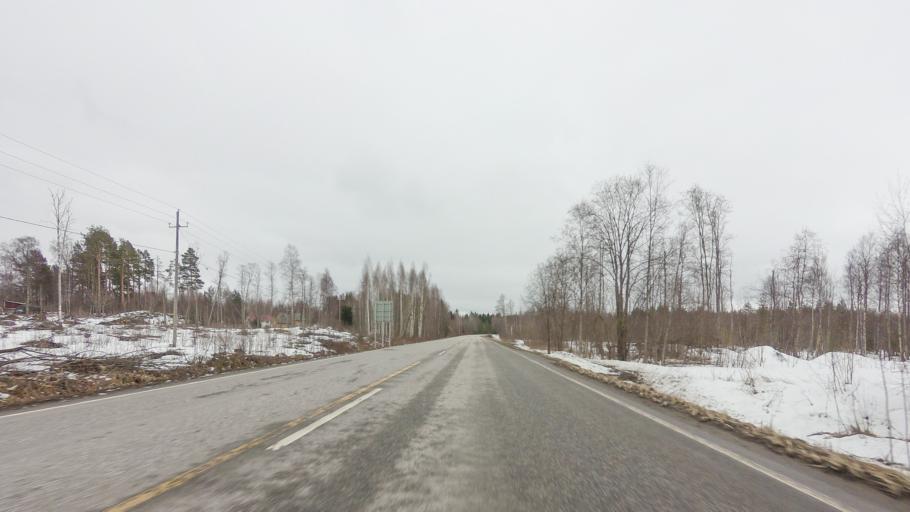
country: FI
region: Southern Savonia
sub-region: Savonlinna
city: Savonlinna
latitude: 61.9112
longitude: 28.9231
